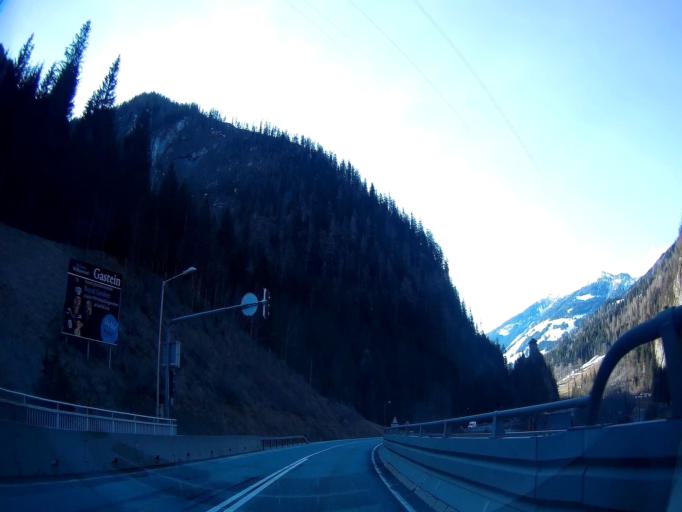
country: AT
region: Salzburg
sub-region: Politischer Bezirk Zell am See
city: Lend
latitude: 47.2896
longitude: 13.0602
